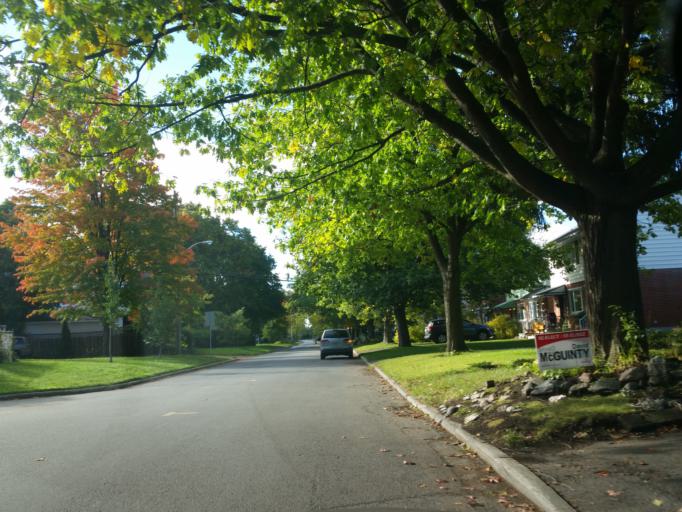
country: CA
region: Ontario
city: Ottawa
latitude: 45.3901
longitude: -75.6691
